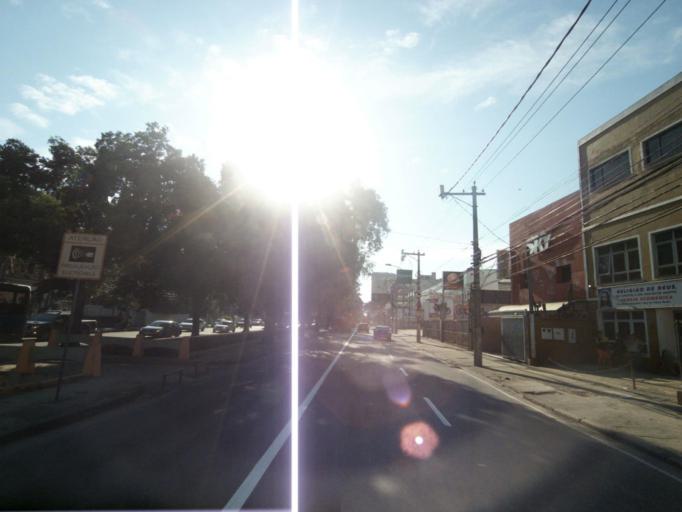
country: BR
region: Rio de Janeiro
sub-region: Niteroi
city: Niteroi
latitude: -22.8810
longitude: -43.0981
